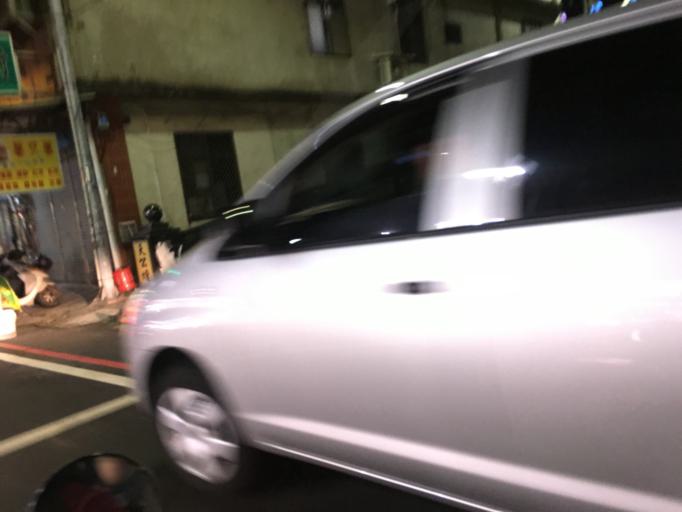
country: TW
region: Taiwan
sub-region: Hsinchu
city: Hsinchu
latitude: 24.8000
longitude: 120.9579
